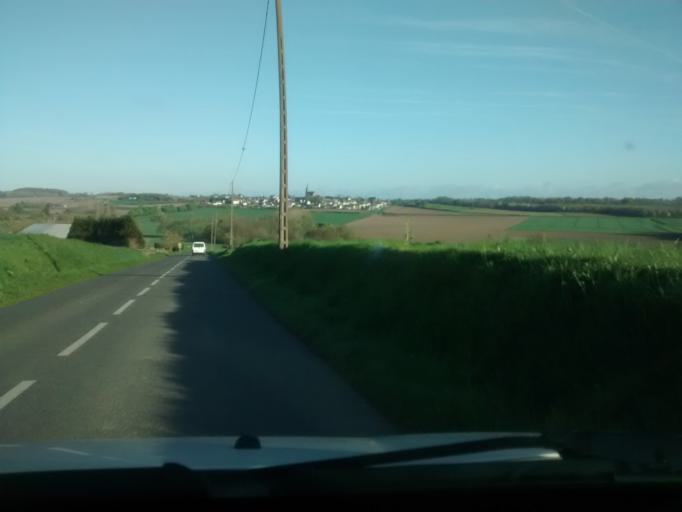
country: FR
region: Brittany
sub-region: Departement d'Ille-et-Vilaine
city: Pleine-Fougeres
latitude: 48.5415
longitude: -1.5711
